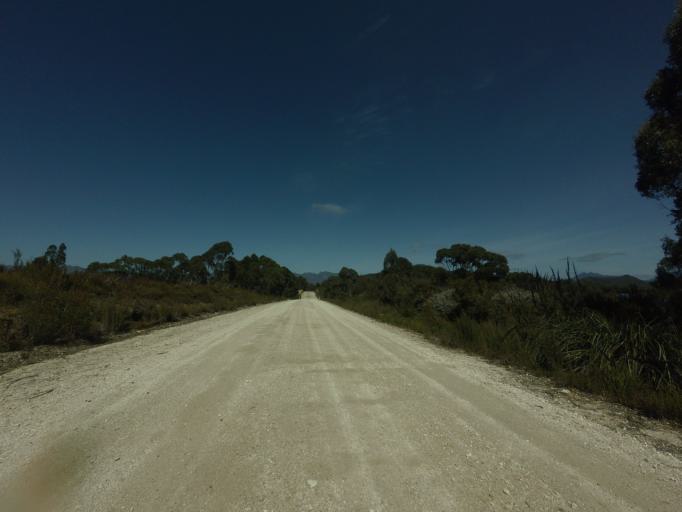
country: AU
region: Tasmania
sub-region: Huon Valley
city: Geeveston
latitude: -43.0266
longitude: 146.3536
